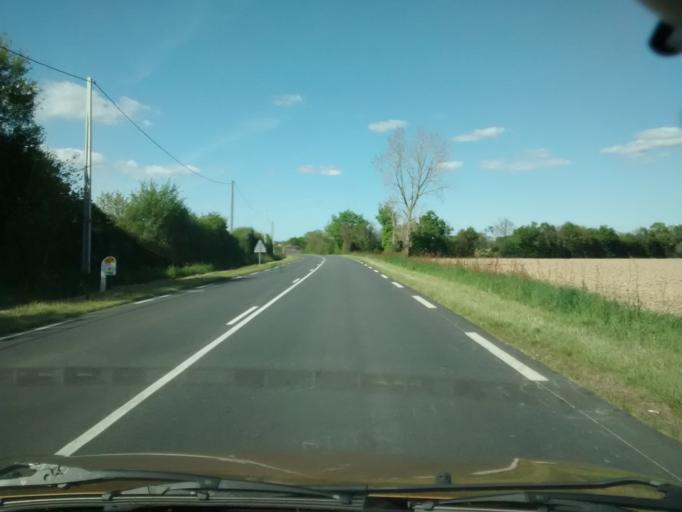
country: FR
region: Pays de la Loire
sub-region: Departement de la Vendee
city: Saint-Philbert-de-Bouaine
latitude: 47.0101
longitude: -1.5051
